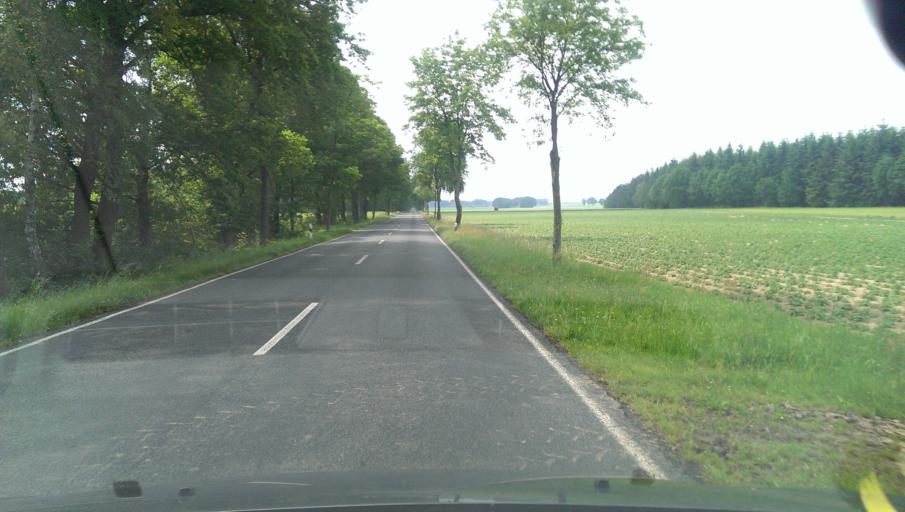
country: DE
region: Lower Saxony
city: Obernholz
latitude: 52.7469
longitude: 10.5482
